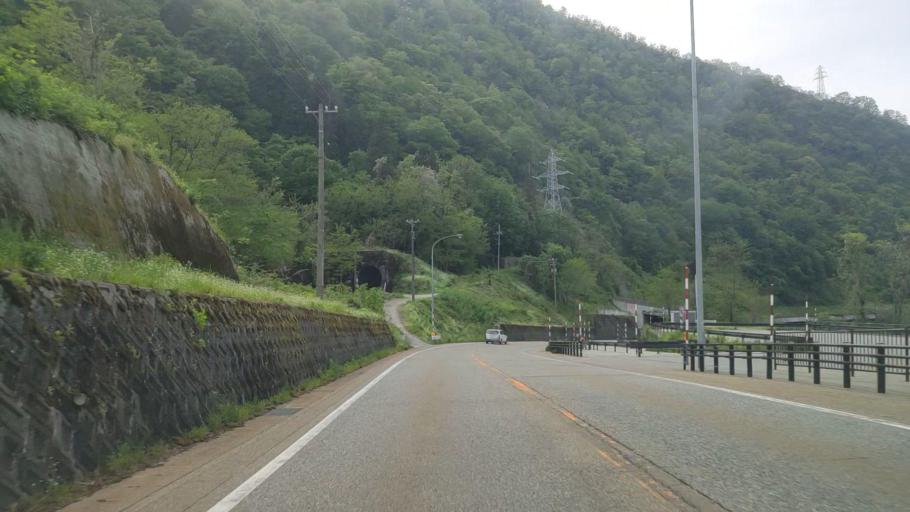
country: JP
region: Gifu
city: Takayama
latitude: 36.3504
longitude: 137.2900
